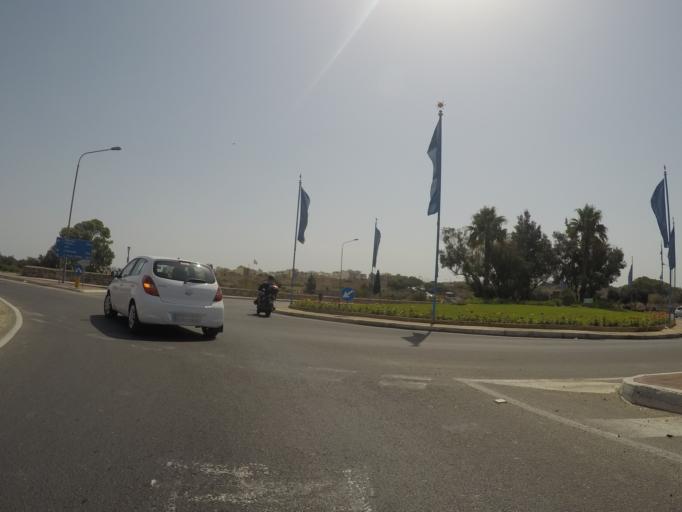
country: MT
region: L-Imtarfa
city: Imtarfa
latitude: 35.9047
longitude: 14.4084
